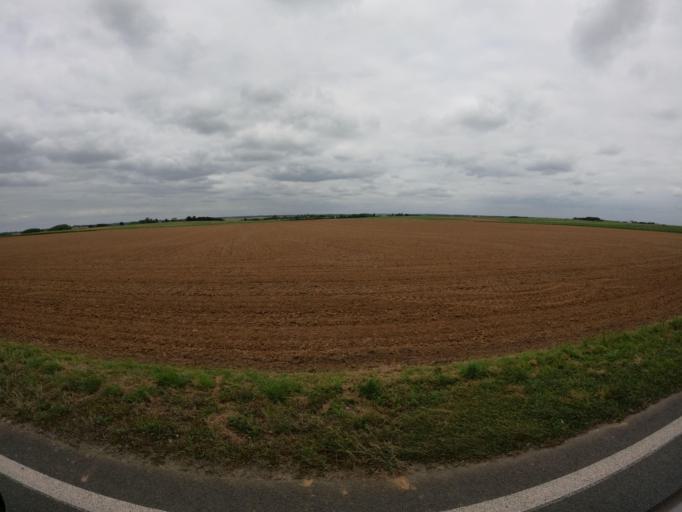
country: FR
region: Pays de la Loire
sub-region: Departement de la Vendee
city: Sainte-Hermine
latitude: 46.5471
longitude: -1.0365
